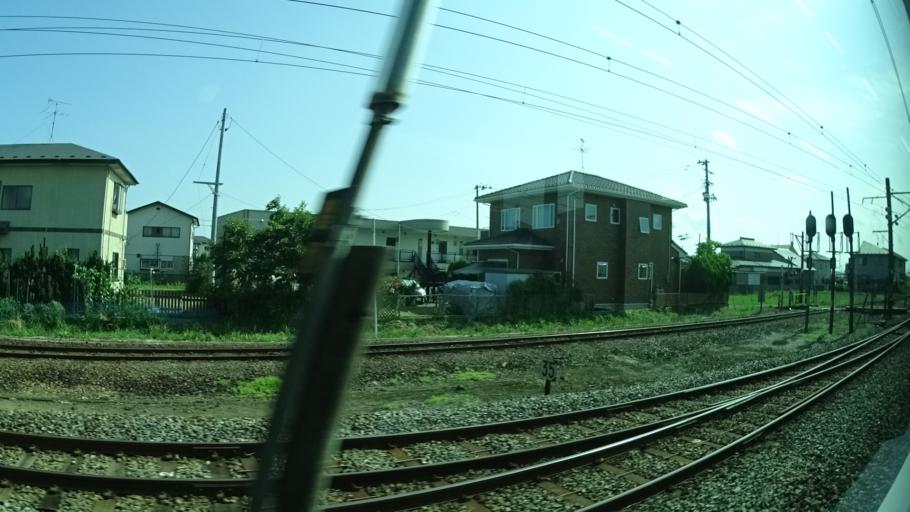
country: JP
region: Miyagi
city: Rifu
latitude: 38.2991
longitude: 140.9753
